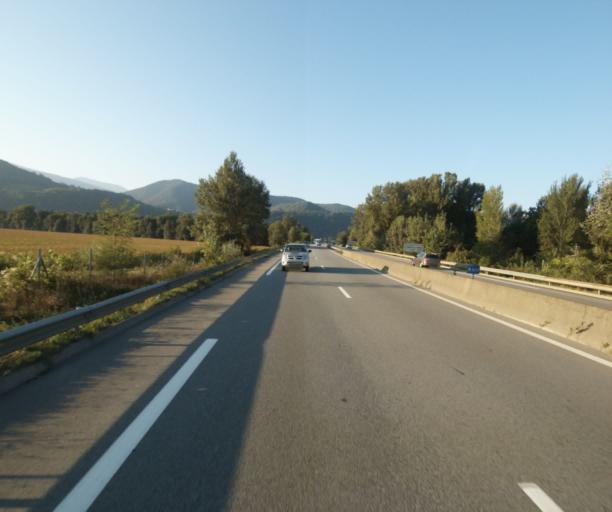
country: FR
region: Rhone-Alpes
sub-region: Departement de l'Isere
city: Gieres
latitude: 45.1945
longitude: 5.7821
